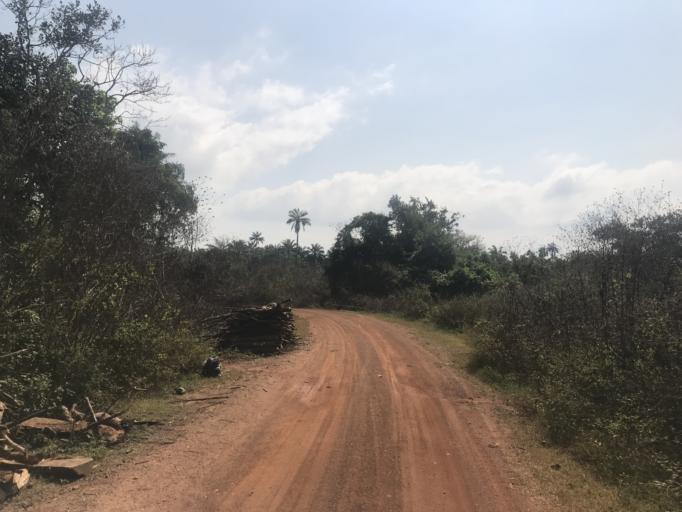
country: NG
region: Osun
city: Ikirun
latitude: 7.8331
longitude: 4.6344
